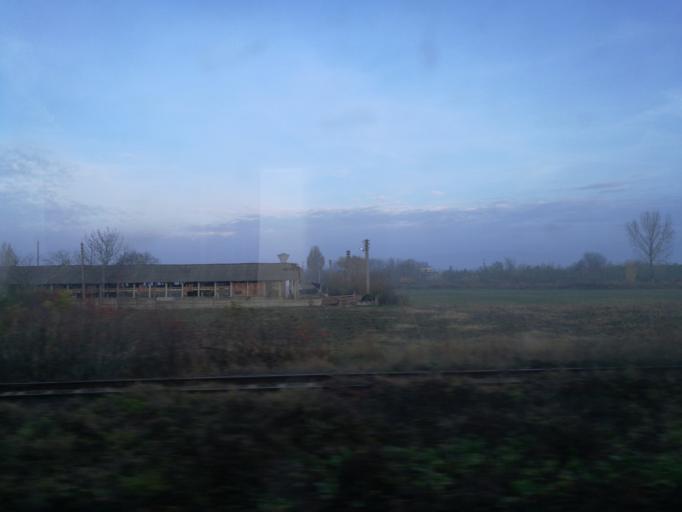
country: RO
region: Buzau
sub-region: Comuna Sahateni
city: Sahateni
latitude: 45.0324
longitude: 26.5256
